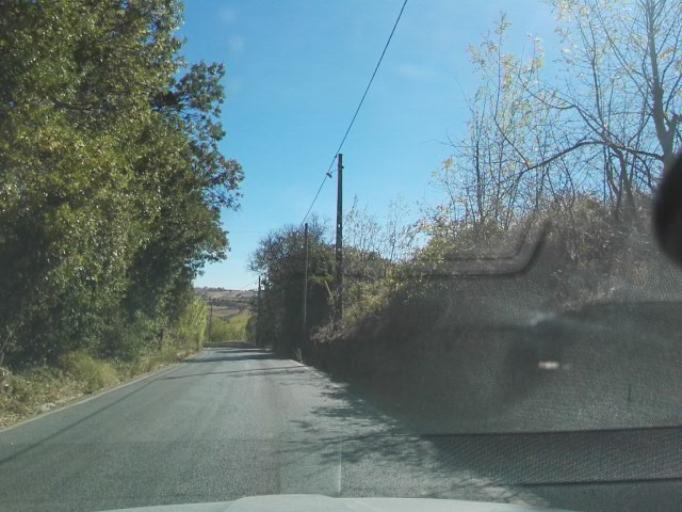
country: PT
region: Lisbon
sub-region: Vila Franca de Xira
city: Sao Joao dos Montes
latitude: 38.9474
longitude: -9.0520
